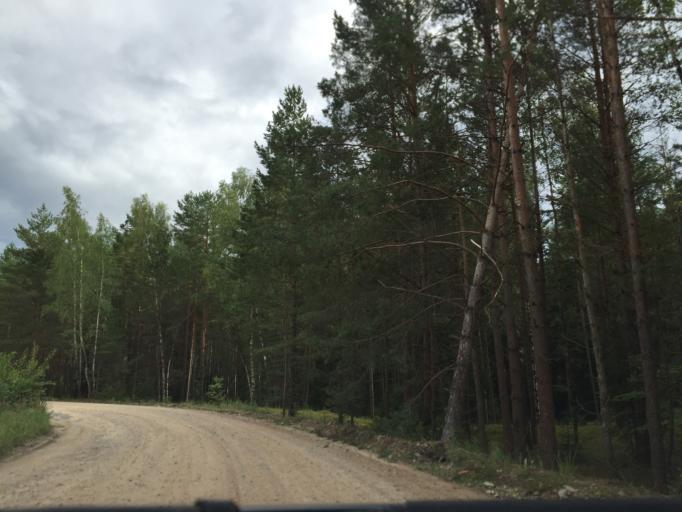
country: LV
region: Saulkrastu
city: Saulkrasti
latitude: 57.1878
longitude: 24.3638
